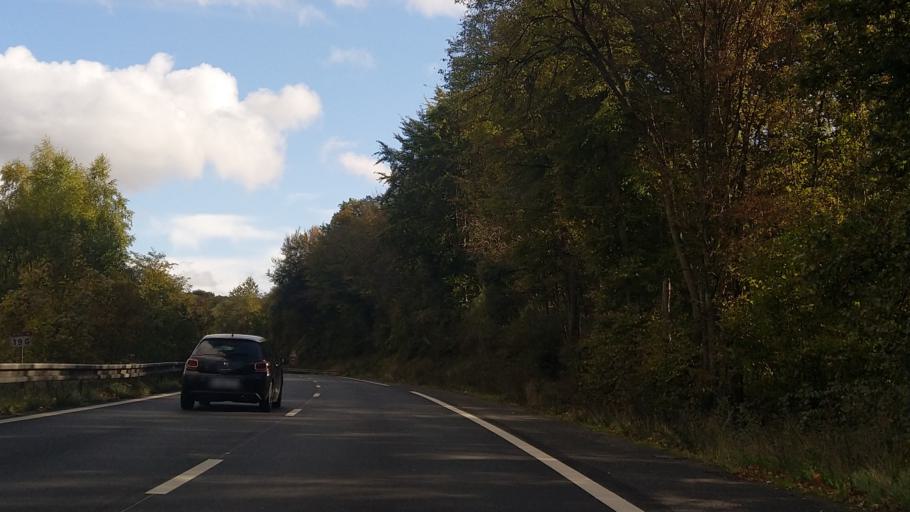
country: FR
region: Ile-de-France
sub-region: Departement du Val-d'Oise
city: Mours
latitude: 49.1050
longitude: 2.2598
